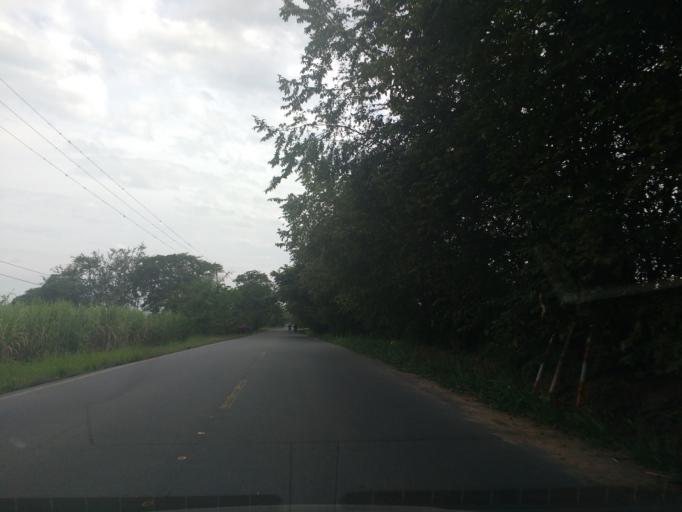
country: CO
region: Valle del Cauca
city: Florida
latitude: 3.2932
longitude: -76.2283
